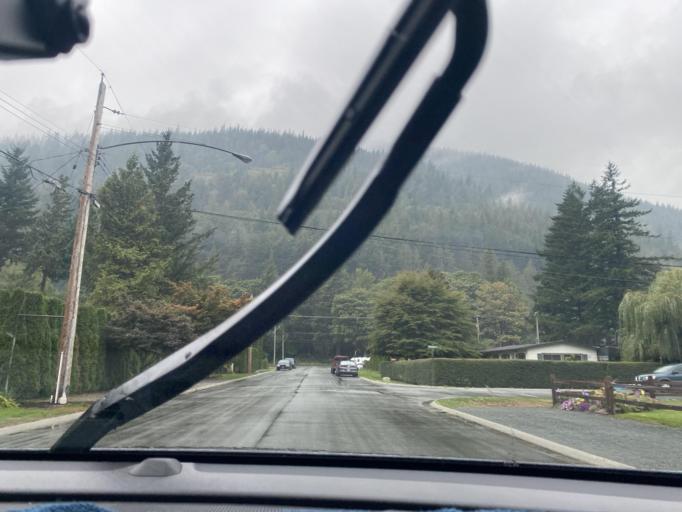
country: CA
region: British Columbia
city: Agassiz
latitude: 49.2882
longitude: -121.7784
